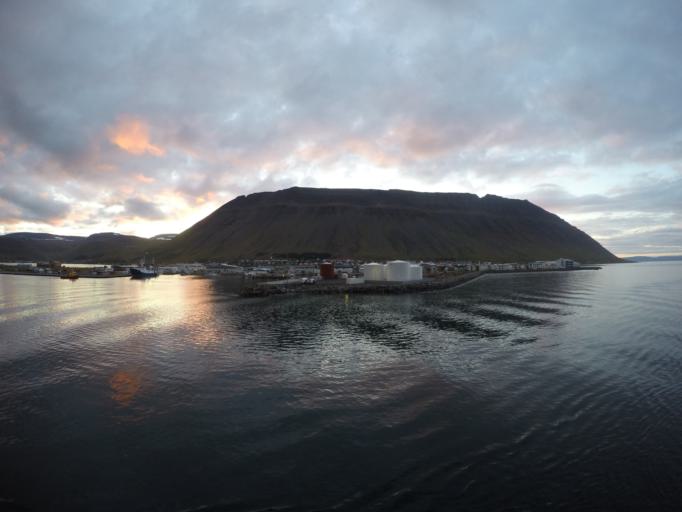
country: IS
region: Westfjords
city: Isafjoerdur
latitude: 66.0673
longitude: -23.1131
